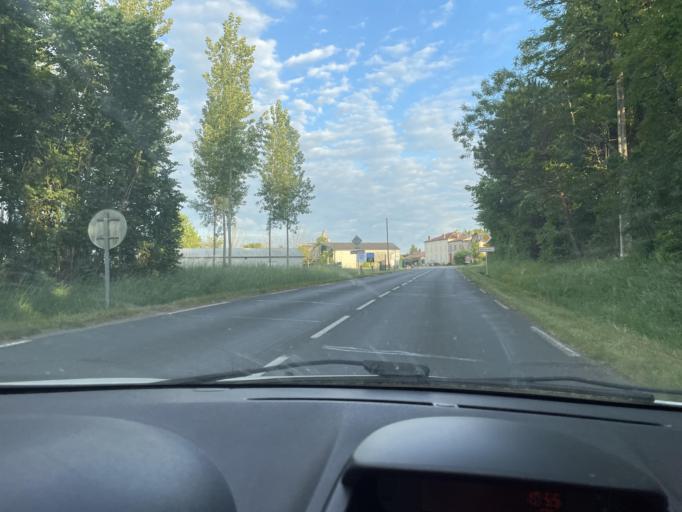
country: FR
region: Aquitaine
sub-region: Departement de la Gironde
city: Grignols
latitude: 44.3543
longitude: 0.0062
